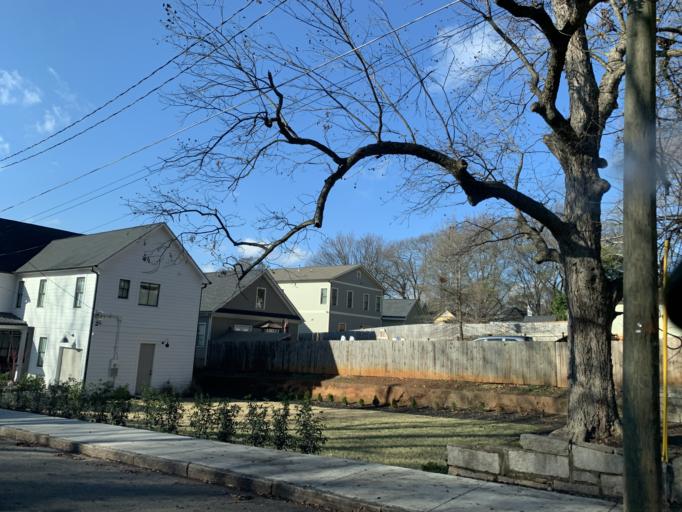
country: US
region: Georgia
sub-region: Fulton County
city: Atlanta
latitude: 33.7355
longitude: -84.3792
